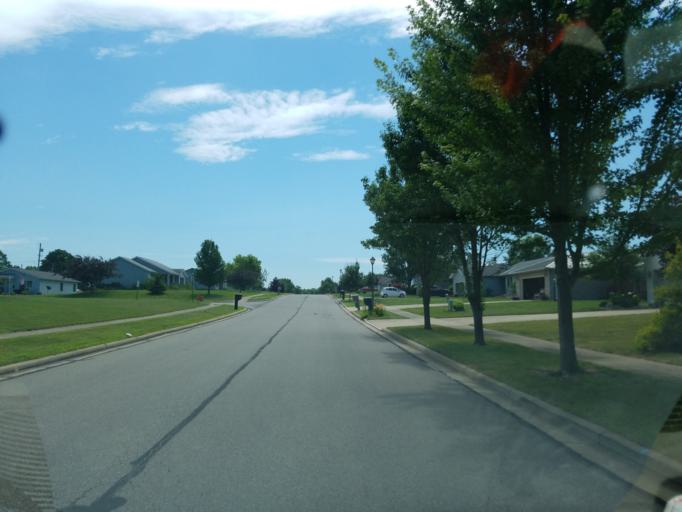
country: US
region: Ohio
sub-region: Ashland County
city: Ashland
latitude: 40.8715
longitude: -82.3389
